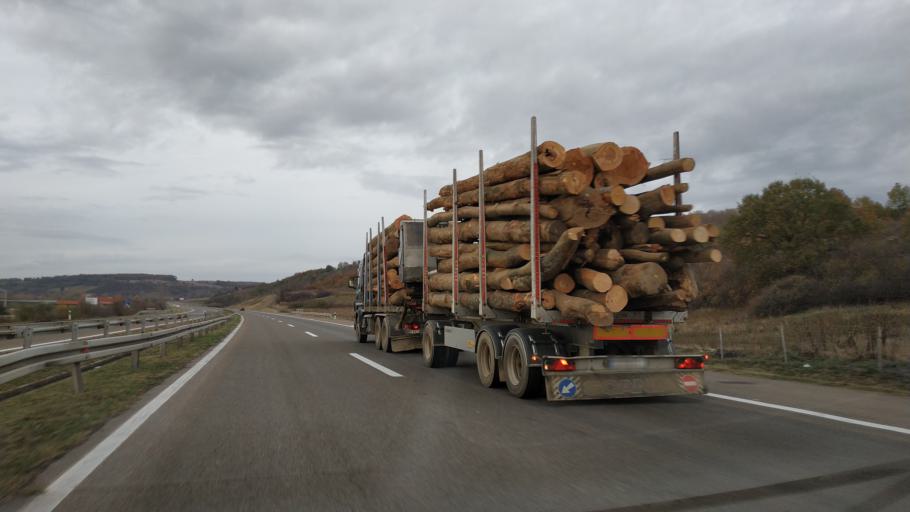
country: RS
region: Central Serbia
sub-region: Nisavski Okrug
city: Aleksinac
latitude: 43.4403
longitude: 21.8007
